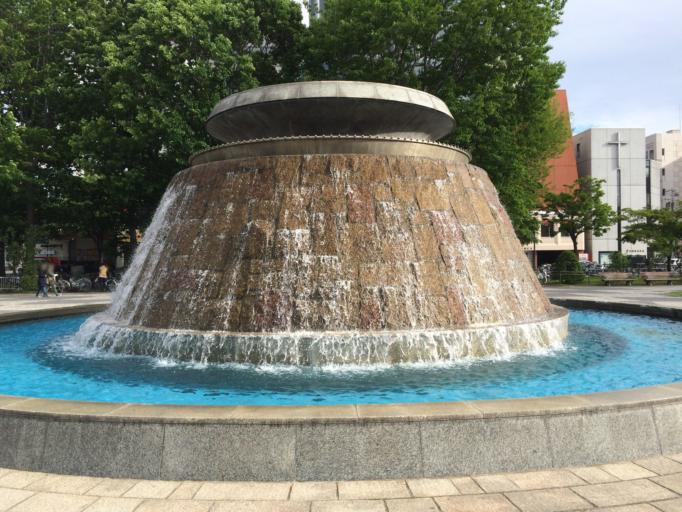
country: JP
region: Hokkaido
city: Sapporo
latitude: 43.0591
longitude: 141.3402
